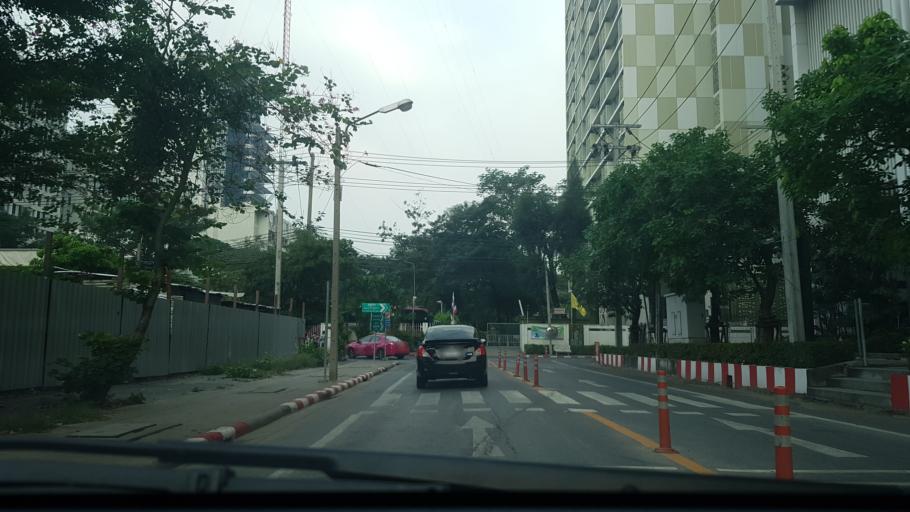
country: TH
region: Bangkok
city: Pathum Wan
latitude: 13.7420
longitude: 100.5253
